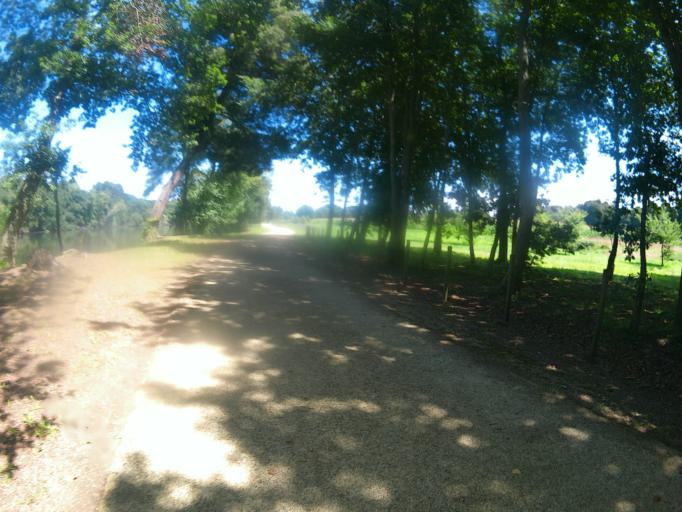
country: PT
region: Viana do Castelo
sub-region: Vila Nova de Cerveira
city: Vila Nova de Cerveira
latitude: 41.9636
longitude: -8.7413
